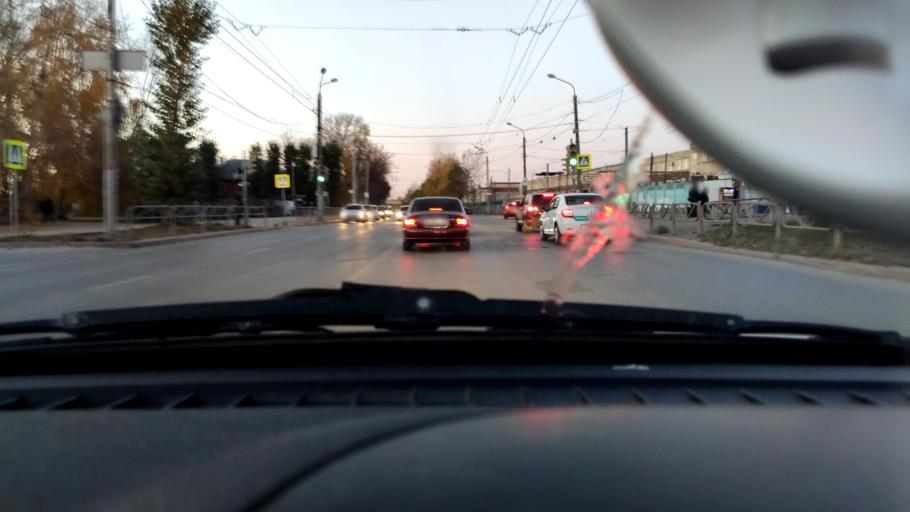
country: RU
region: Perm
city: Perm
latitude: 57.9719
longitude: 56.2461
